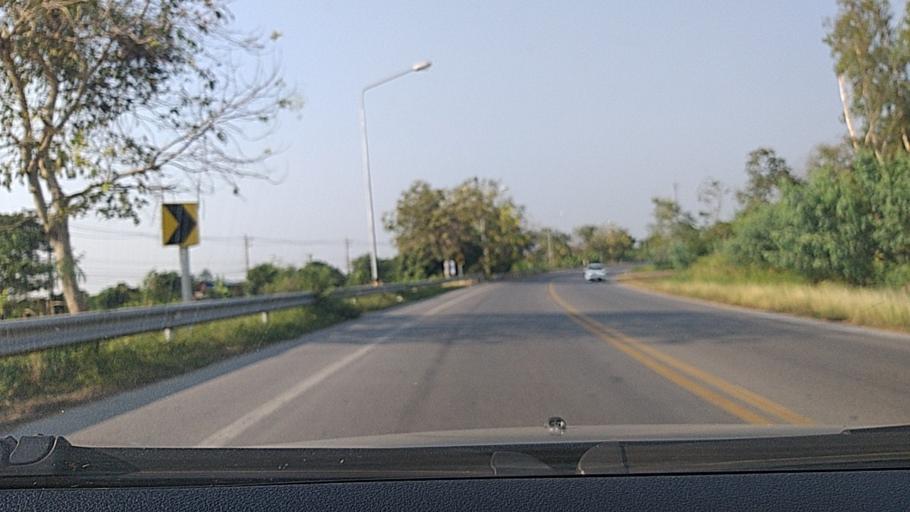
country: TH
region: Sing Buri
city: Phrom Buri
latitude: 14.8221
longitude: 100.4287
